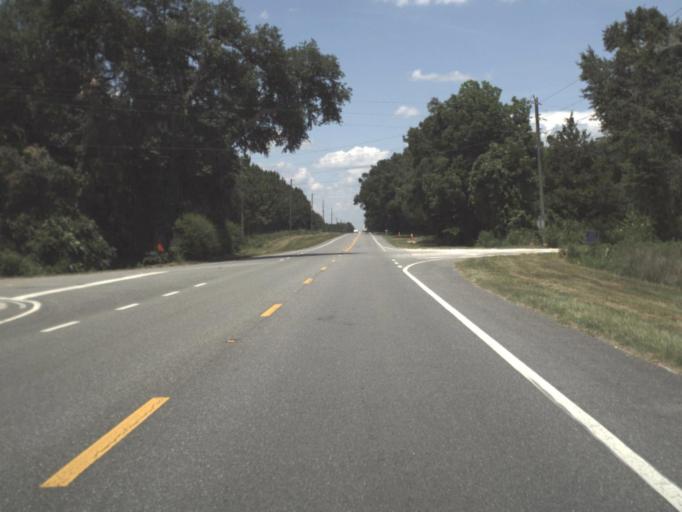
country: US
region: Florida
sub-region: Suwannee County
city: Wellborn
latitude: 30.0737
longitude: -82.7756
